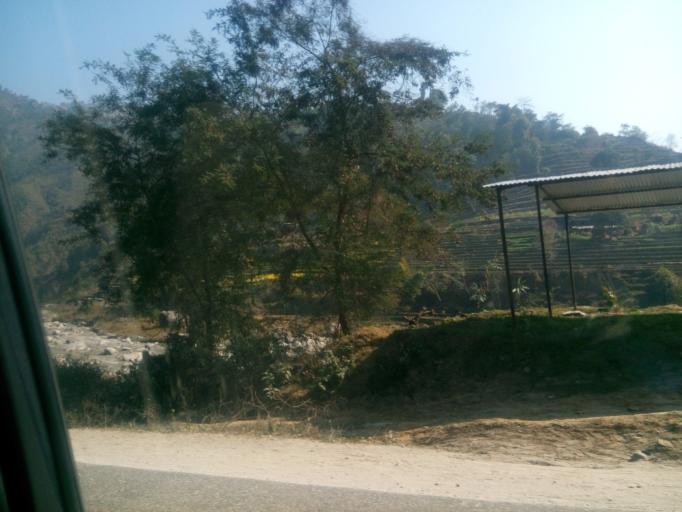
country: NP
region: Central Region
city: Kirtipur
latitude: 27.7596
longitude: 85.0436
